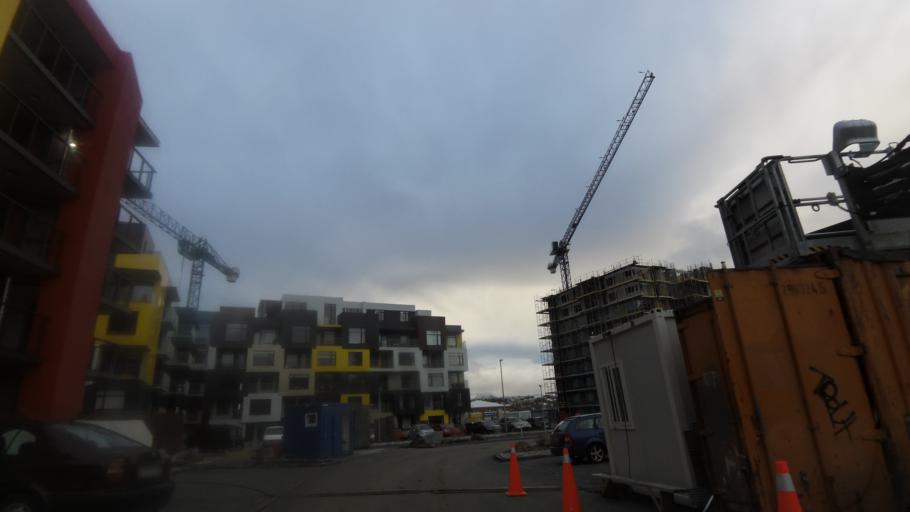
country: IS
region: Capital Region
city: Kopavogur
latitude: 64.0980
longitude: -21.8790
